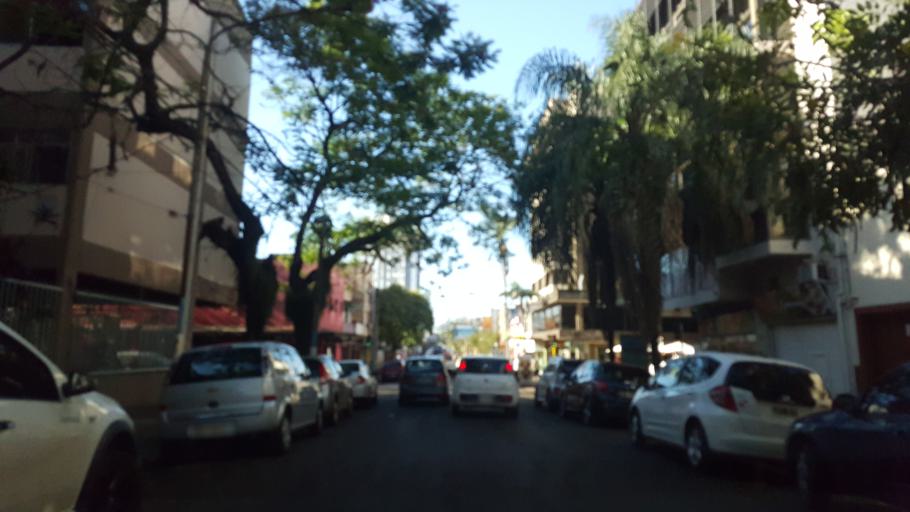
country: AR
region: Misiones
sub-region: Departamento de Capital
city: Posadas
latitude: -27.3701
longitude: -55.8962
